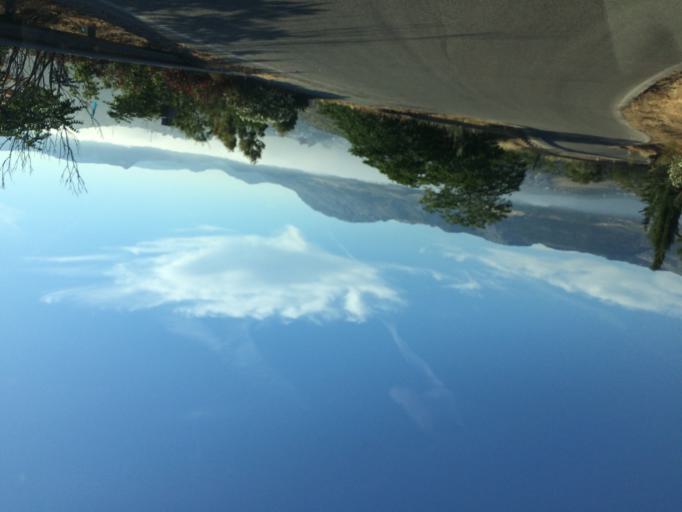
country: ES
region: Andalusia
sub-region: Provincia de Malaga
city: Colmenar
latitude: 36.8912
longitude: -4.3419
